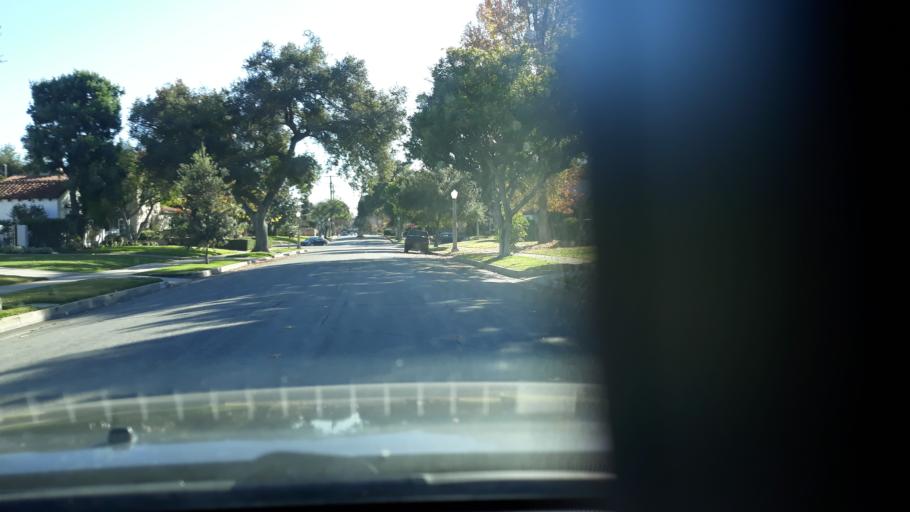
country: US
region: California
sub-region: Los Angeles County
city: San Marino
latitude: 34.1156
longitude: -118.1114
